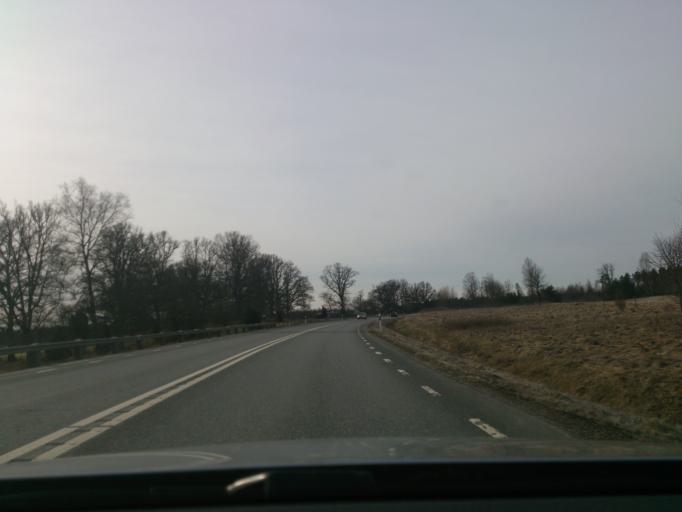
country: SE
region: Kronoberg
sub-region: Alvesta Kommun
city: Moheda
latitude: 56.9593
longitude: 14.5723
